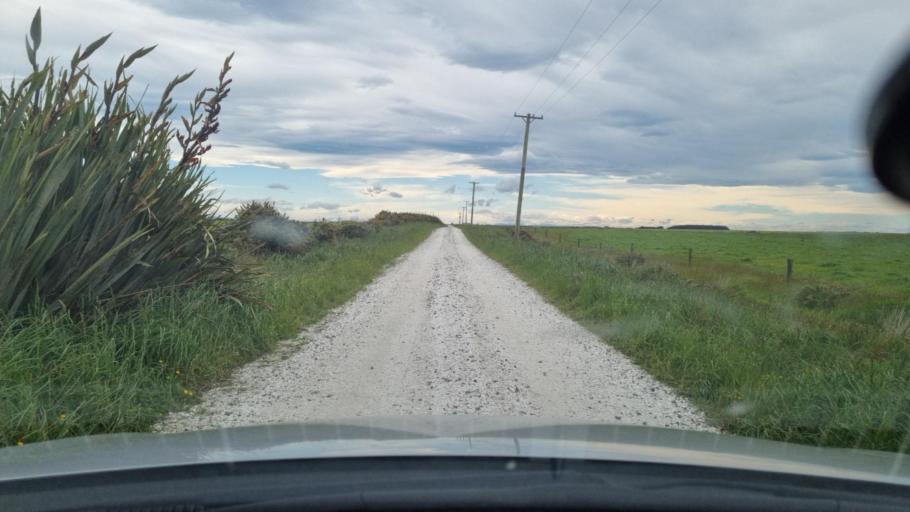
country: NZ
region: Southland
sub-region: Invercargill City
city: Bluff
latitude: -46.5333
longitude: 168.3859
